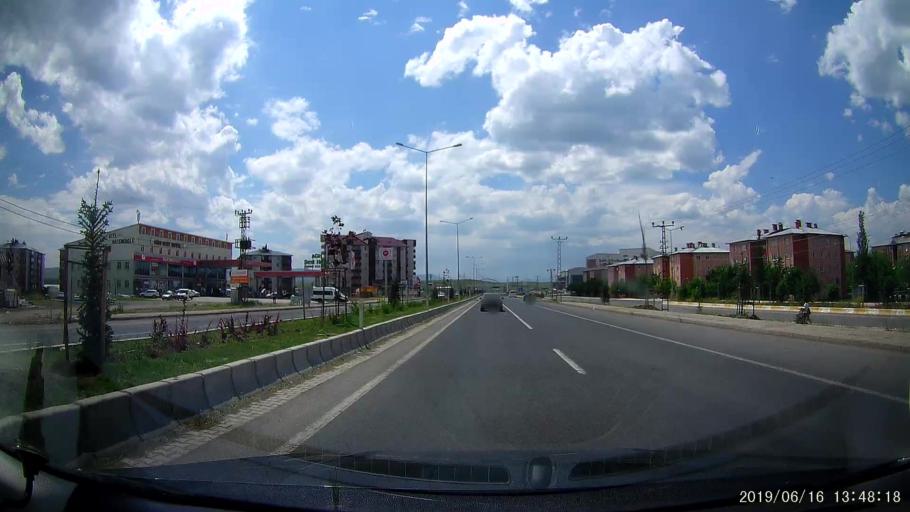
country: TR
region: Agri
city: Agri
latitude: 39.7144
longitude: 43.0097
